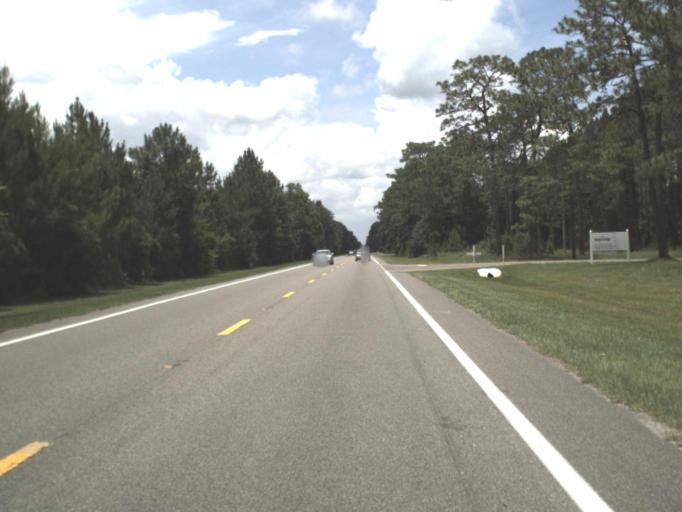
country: US
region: Florida
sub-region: Nassau County
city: Yulee
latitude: 30.6678
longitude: -81.6386
